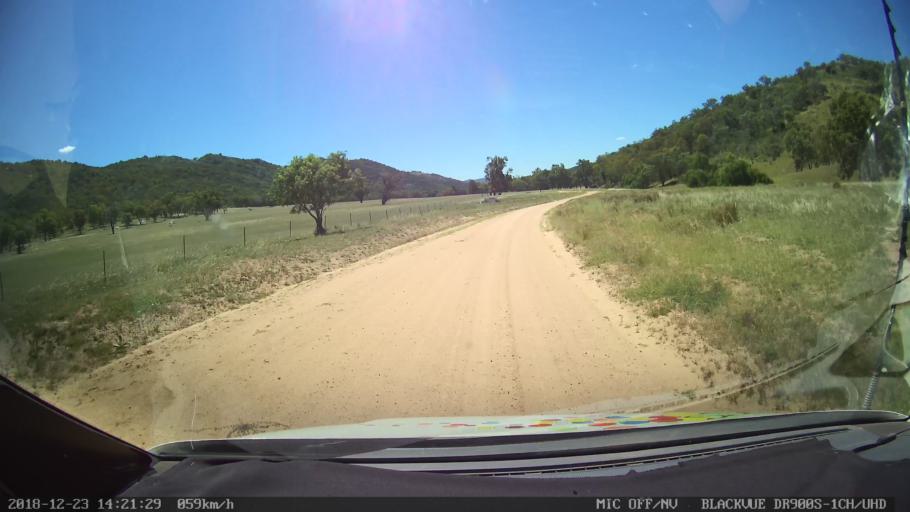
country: AU
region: New South Wales
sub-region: Tamworth Municipality
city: Manilla
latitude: -30.6466
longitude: 150.9803
